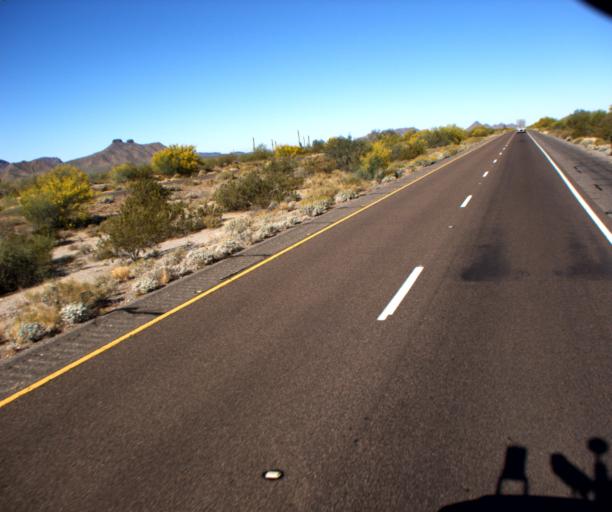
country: US
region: Arizona
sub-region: Maricopa County
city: Gila Bend
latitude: 32.8662
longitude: -112.4168
